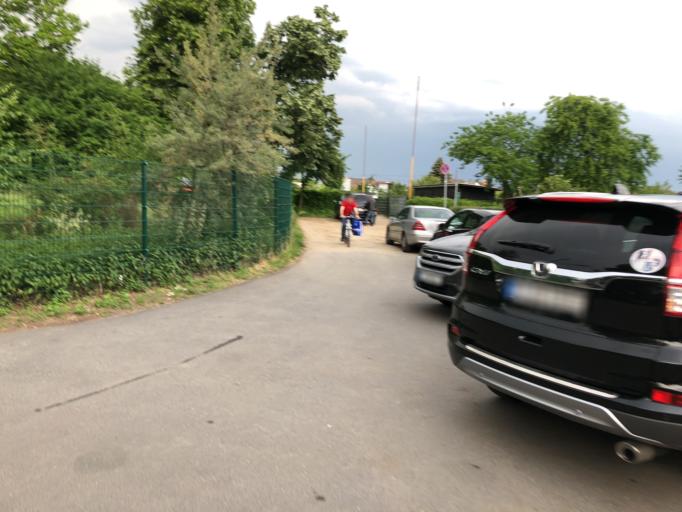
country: DE
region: Hesse
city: Niederrad
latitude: 50.0791
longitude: 8.6141
